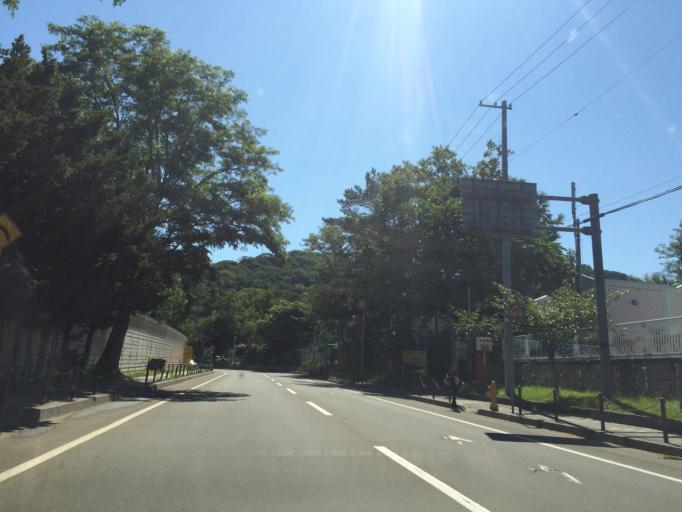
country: JP
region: Hokkaido
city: Sapporo
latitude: 43.0513
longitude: 141.3051
